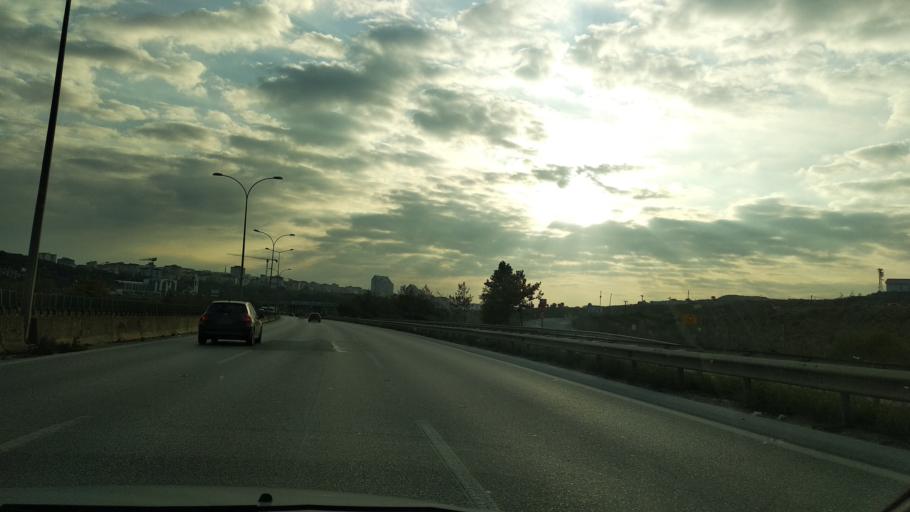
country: TR
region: Istanbul
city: Icmeler
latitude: 40.8819
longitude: 29.3174
